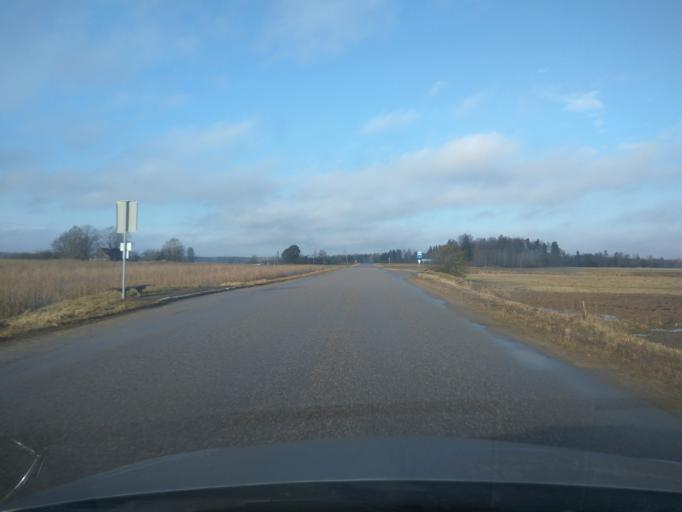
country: LV
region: Saldus Rajons
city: Saldus
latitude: 56.8220
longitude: 22.3773
